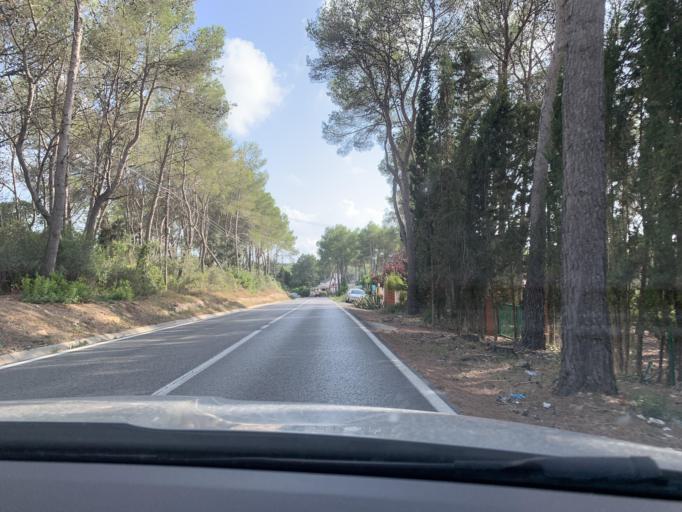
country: ES
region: Catalonia
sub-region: Provincia de Tarragona
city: el Catllar
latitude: 41.1573
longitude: 1.3146
